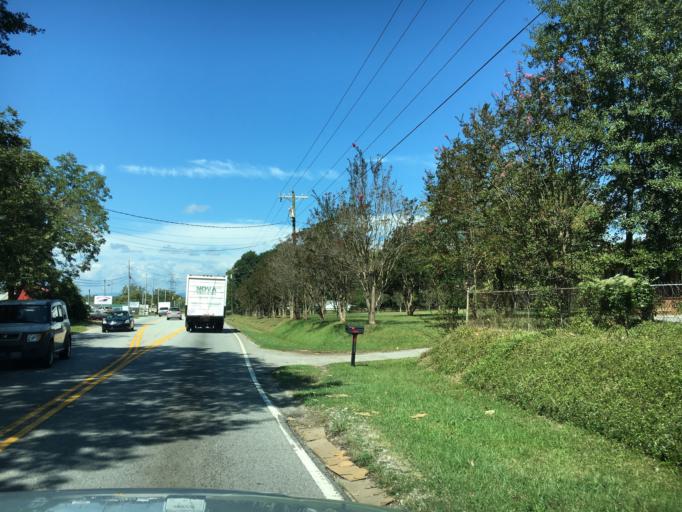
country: US
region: South Carolina
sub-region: Greenville County
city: Taylors
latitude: 34.9551
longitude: -82.2960
